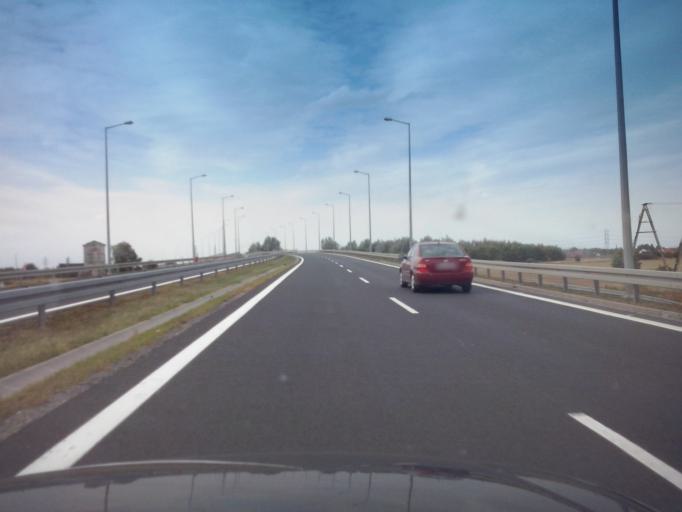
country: PL
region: Subcarpathian Voivodeship
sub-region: Powiat stalowowolski
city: Stalowa Wola
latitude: 50.6073
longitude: 22.0302
